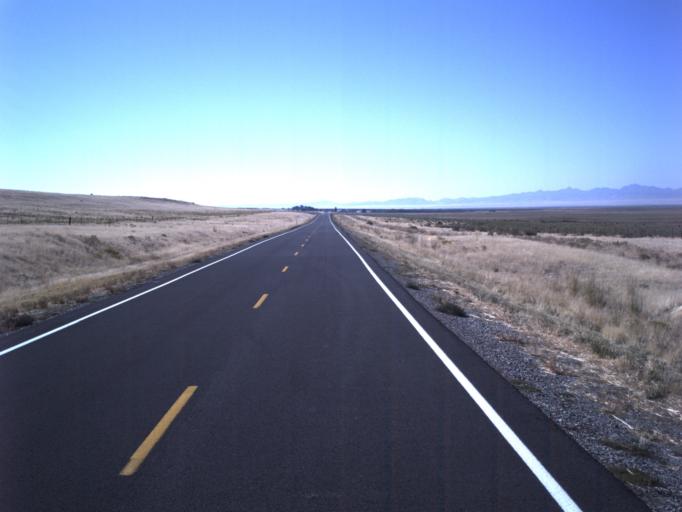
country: US
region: Utah
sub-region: Tooele County
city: Grantsville
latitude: 40.5645
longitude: -112.7336
